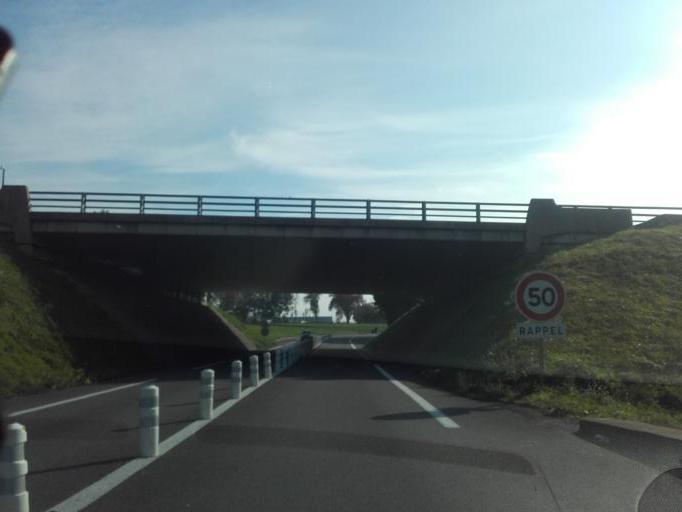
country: FR
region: Bourgogne
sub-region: Departement de Saone-et-Loire
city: Charnay-les-Macon
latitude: 46.2849
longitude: 4.7886
